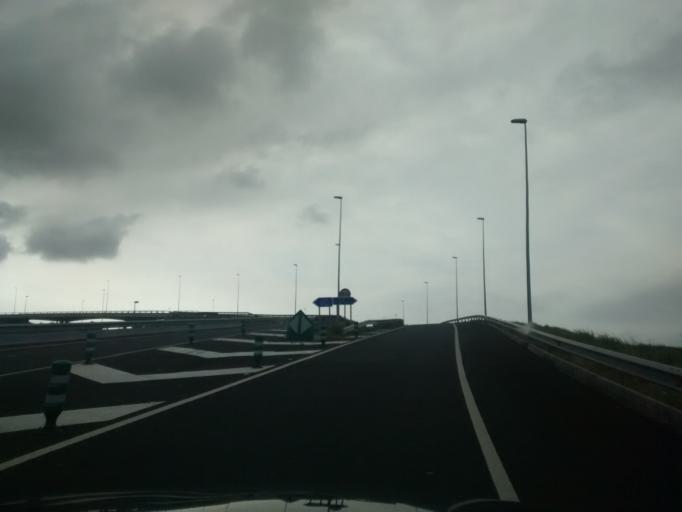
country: ES
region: Cantabria
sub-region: Provincia de Cantabria
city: Santa Cruz de Bezana
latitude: 43.4368
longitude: -3.8736
